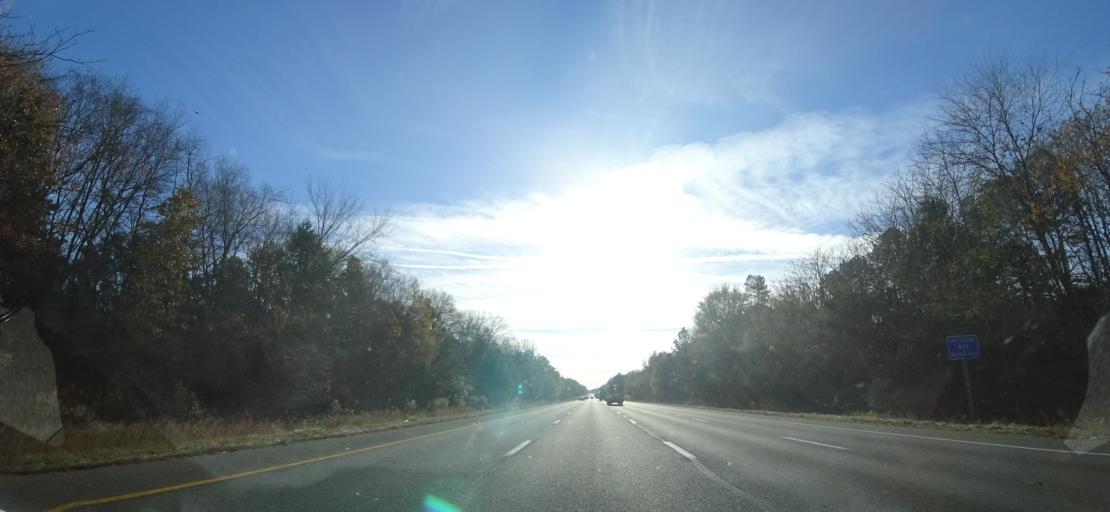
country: US
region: Virginia
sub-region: Hanover County
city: Mechanicsville
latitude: 37.5947
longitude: -77.3484
